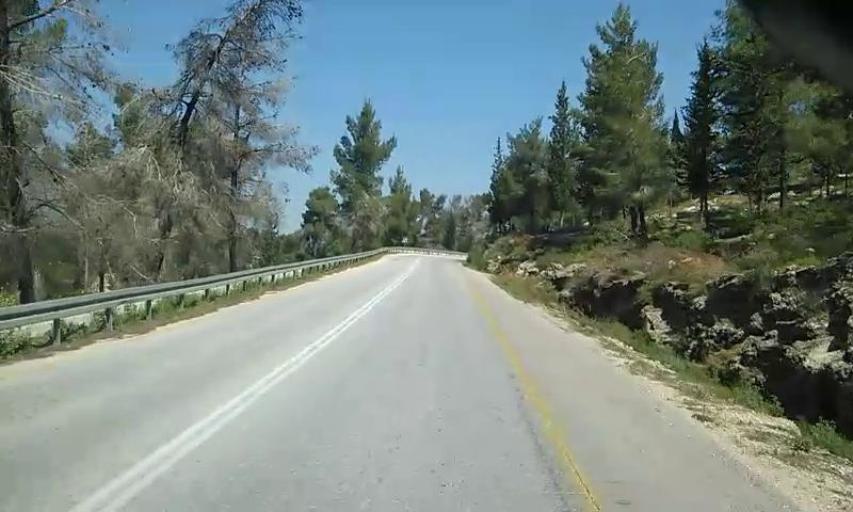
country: PS
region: West Bank
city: Nahhalin
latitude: 31.6741
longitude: 35.0954
